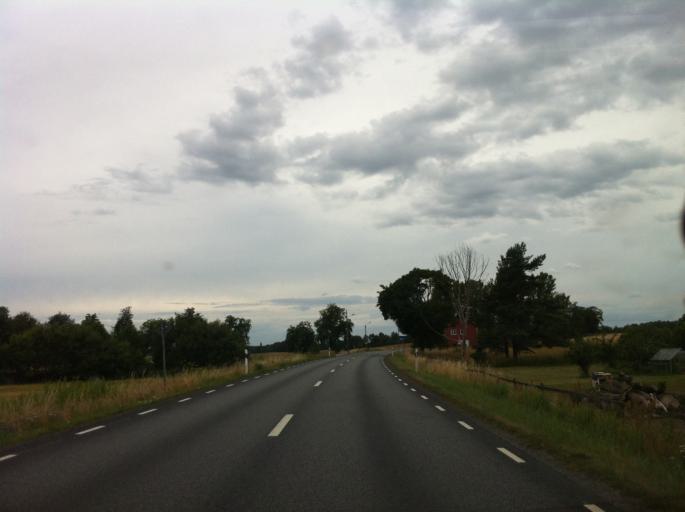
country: SE
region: Skane
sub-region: Hassleholms Kommun
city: Vinslov
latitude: 56.1861
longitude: 13.8868
